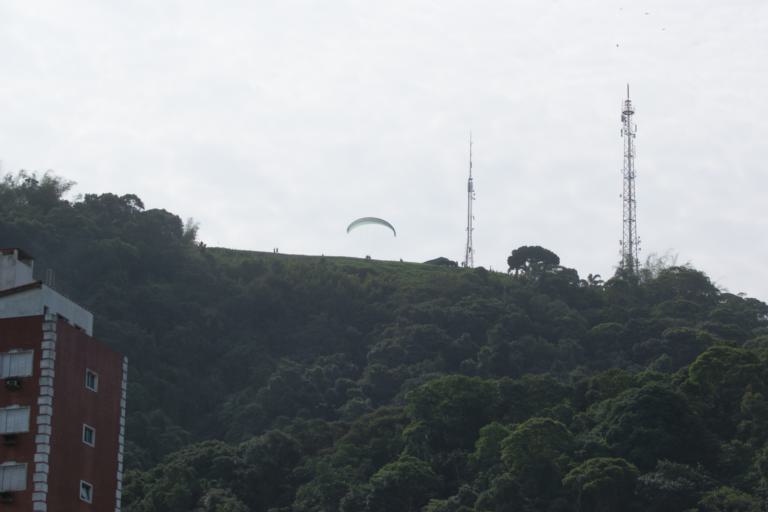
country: BR
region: Sao Paulo
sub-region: Santos
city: Santos
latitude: -23.9693
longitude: -46.3587
